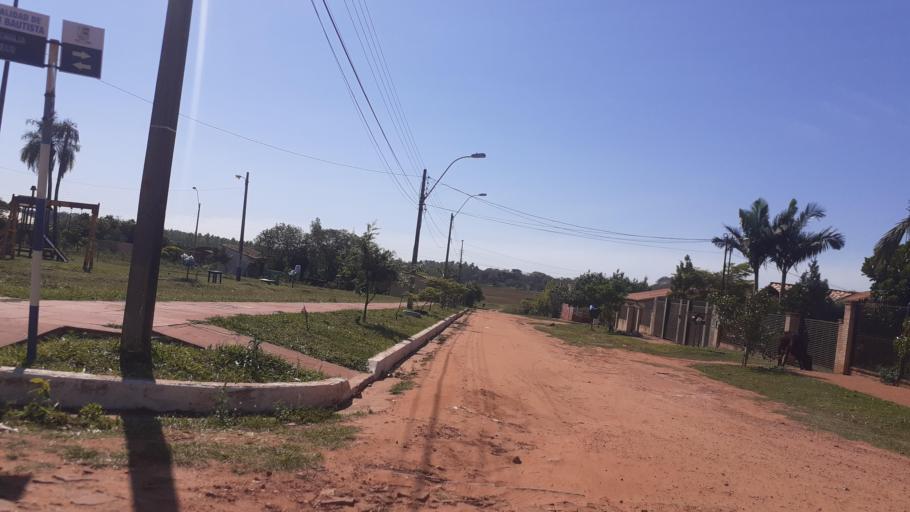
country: PY
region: Misiones
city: San Juan Bautista
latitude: -26.6661
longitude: -57.1255
